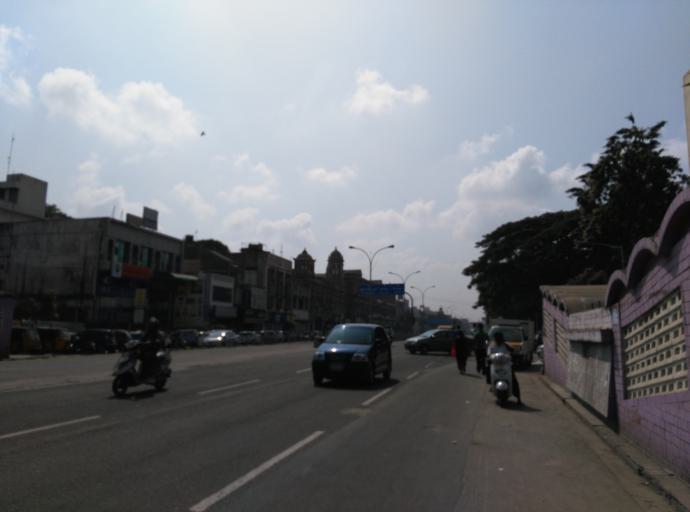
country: IN
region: Tamil Nadu
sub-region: Chennai
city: Chetput
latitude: 13.0635
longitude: 80.2646
